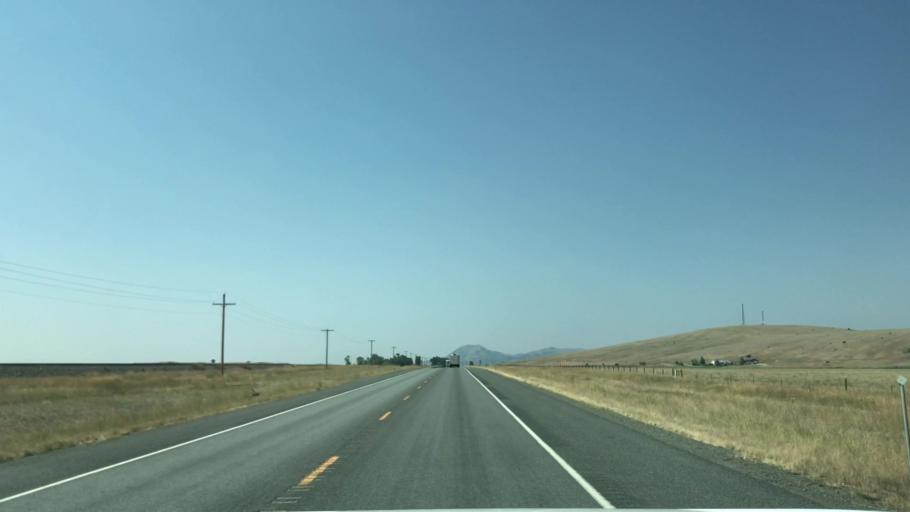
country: US
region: Montana
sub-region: Broadwater County
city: Townsend
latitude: 46.4589
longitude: -111.6412
